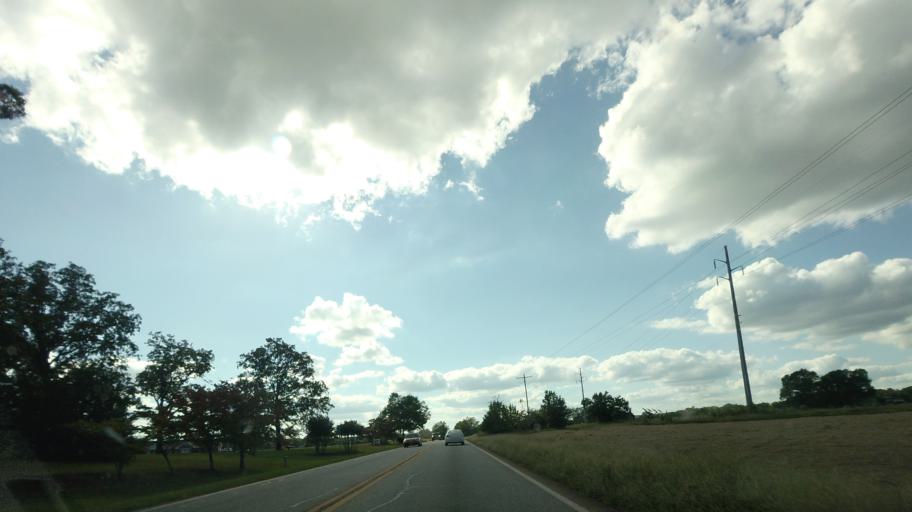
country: US
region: Georgia
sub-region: Lamar County
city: Barnesville
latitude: 33.0543
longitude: -84.0926
